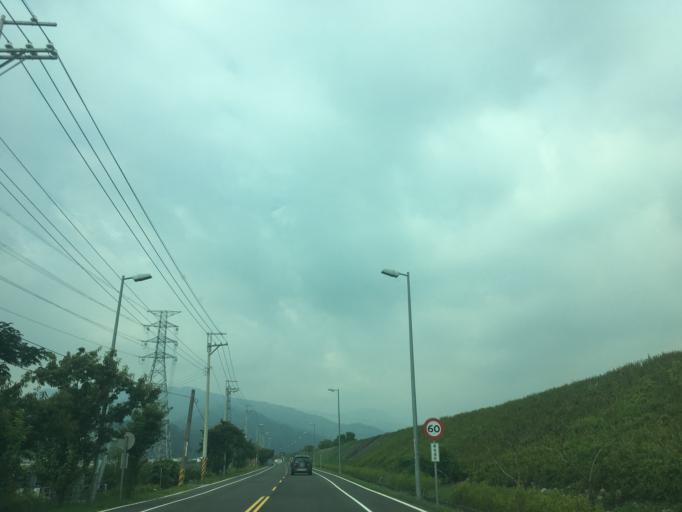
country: TW
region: Taiwan
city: Fengyuan
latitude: 24.2903
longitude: 120.8582
